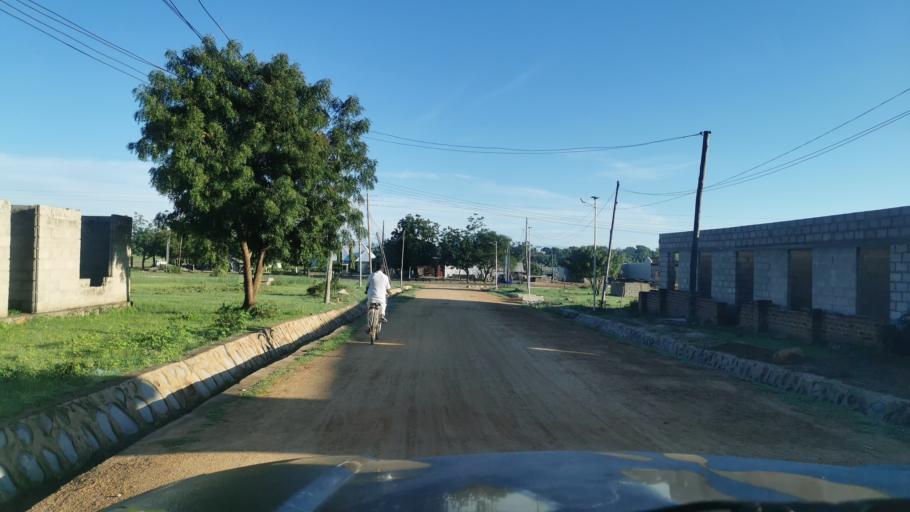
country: TZ
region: Shinyanga
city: Kahama
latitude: -3.8367
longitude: 32.6242
